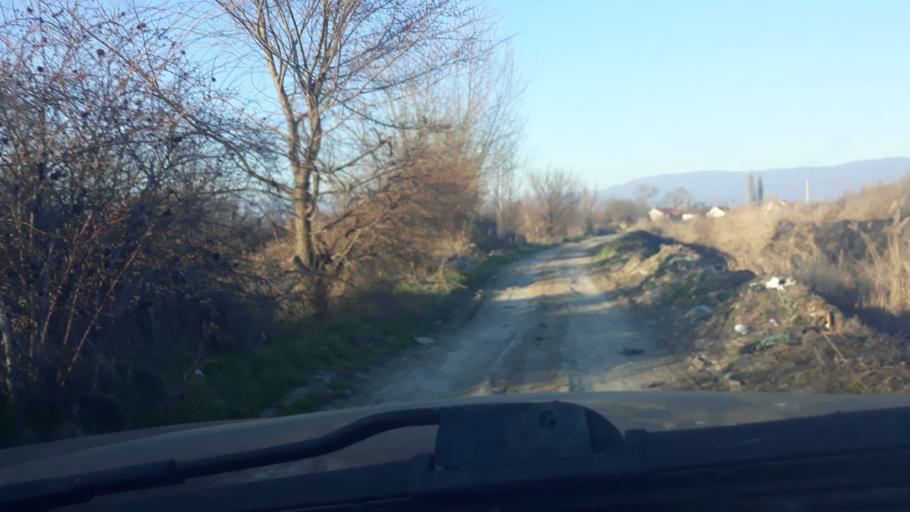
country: MK
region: Strumica
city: Strumica
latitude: 41.4427
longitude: 22.6265
